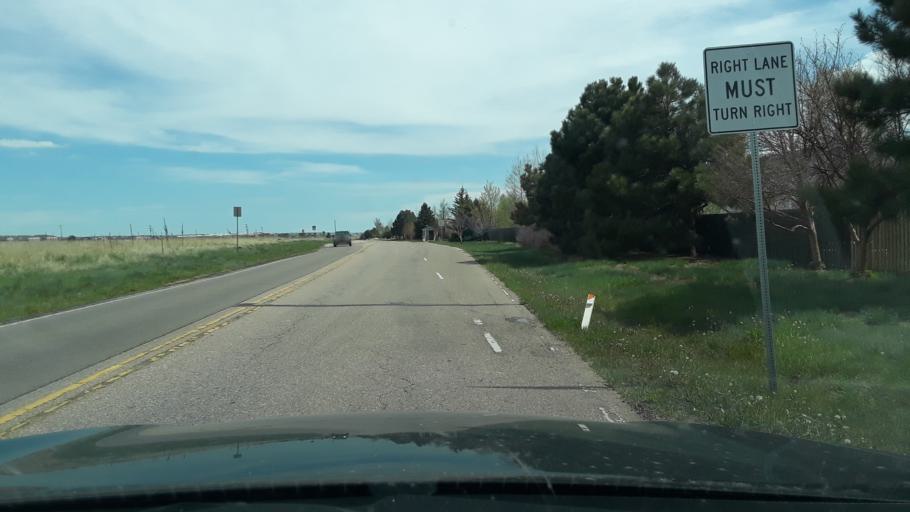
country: US
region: Colorado
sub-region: El Paso County
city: Monument
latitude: 39.0819
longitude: -104.8660
